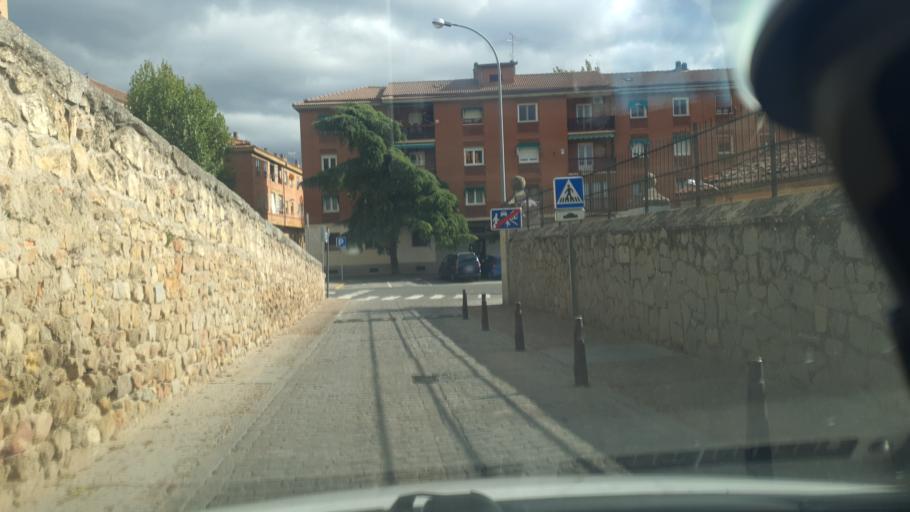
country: ES
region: Castille and Leon
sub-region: Provincia de Segovia
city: Segovia
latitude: 40.9482
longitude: -4.1238
